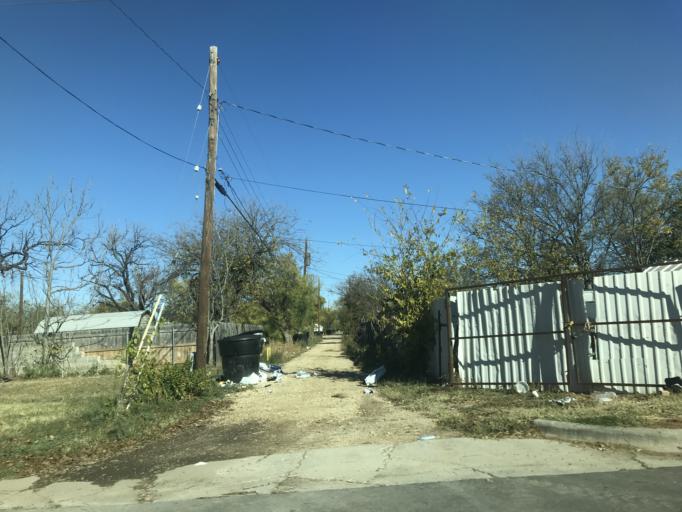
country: US
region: Texas
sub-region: Taylor County
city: Abilene
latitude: 32.4580
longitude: -99.7473
